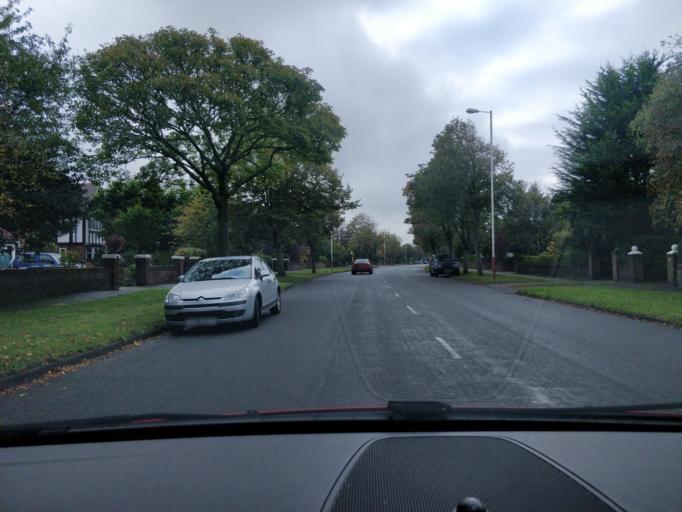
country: GB
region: England
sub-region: Sefton
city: Southport
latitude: 53.6165
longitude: -3.0209
